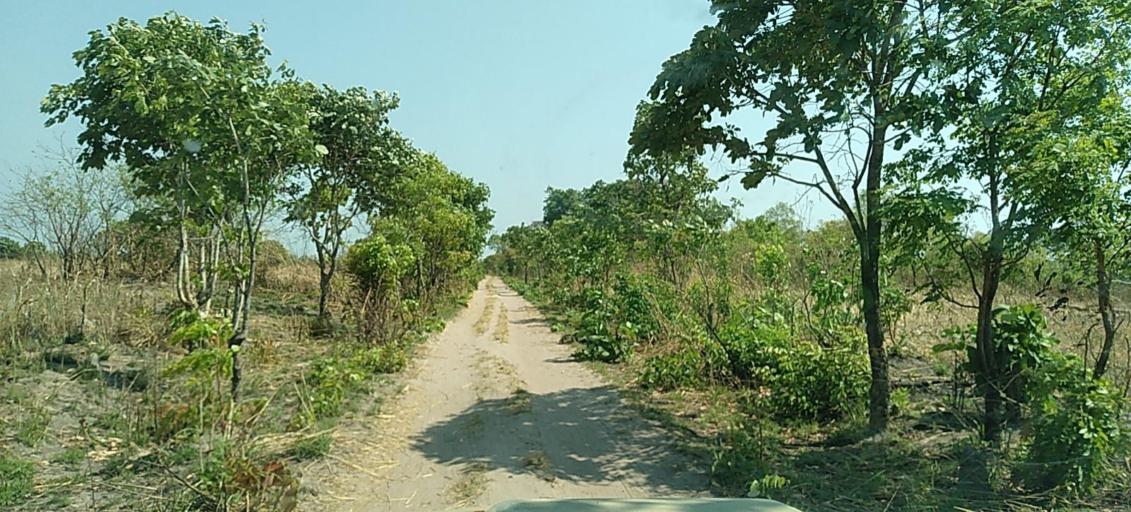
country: ZM
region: North-Western
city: Kalengwa
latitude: -13.2391
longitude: 24.7555
